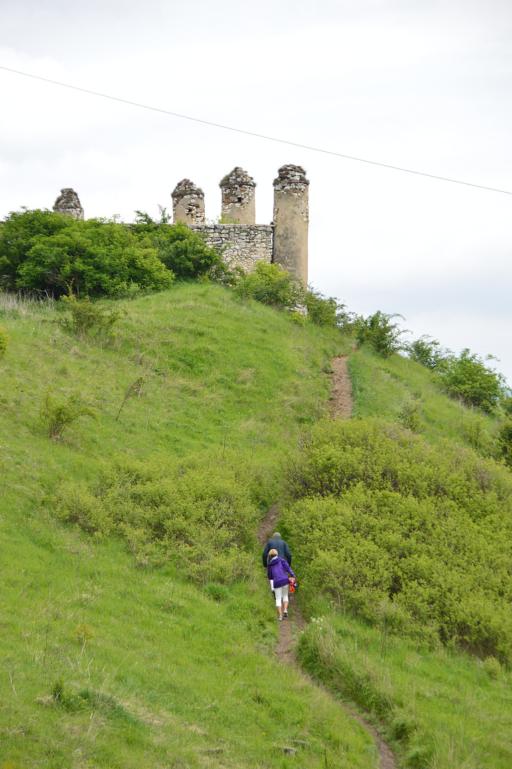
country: SK
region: Presovsky
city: Spisske Podhradie
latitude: 48.9986
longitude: 20.7674
